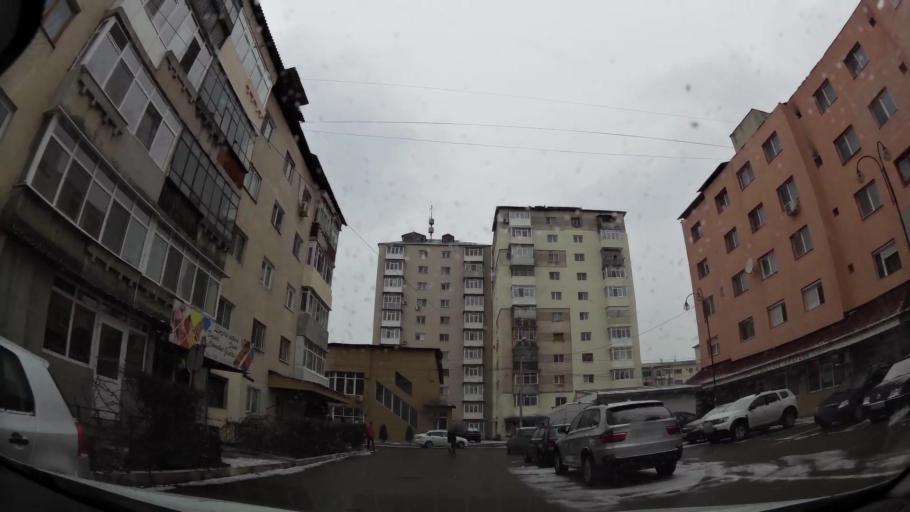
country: RO
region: Dambovita
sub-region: Municipiul Targoviste
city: Targoviste
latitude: 44.9314
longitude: 25.4488
